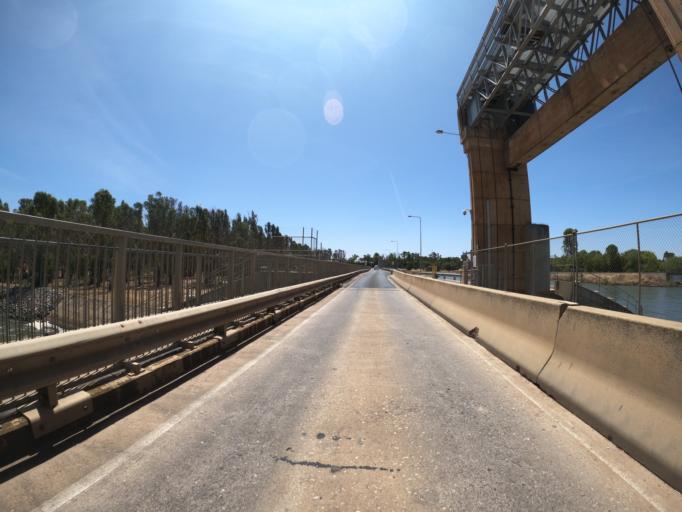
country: AU
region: Victoria
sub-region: Moira
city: Yarrawonga
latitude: -36.0091
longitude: 145.9994
